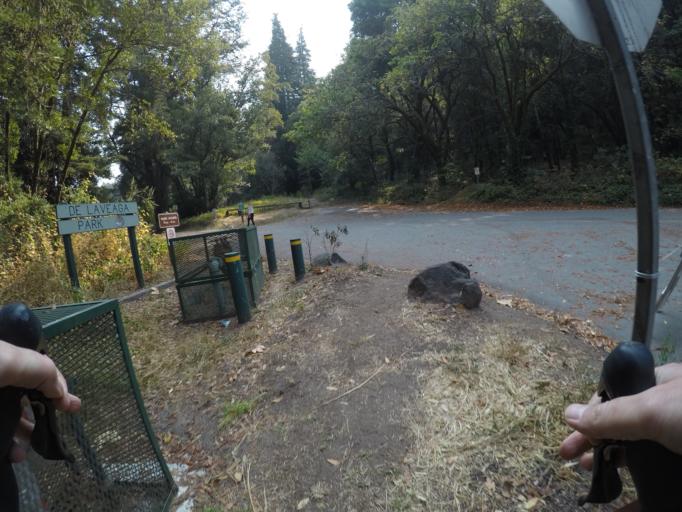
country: US
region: California
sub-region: Santa Cruz County
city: Pasatiempo
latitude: 36.9990
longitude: -122.0048
